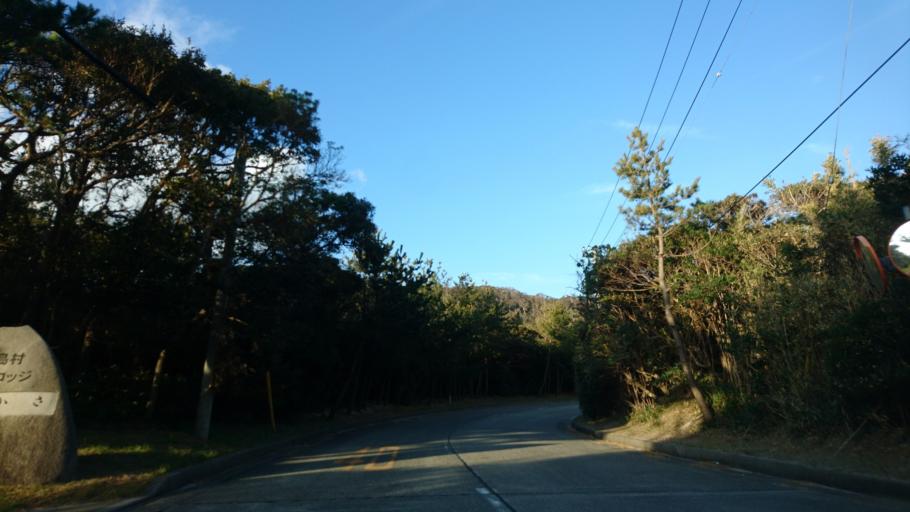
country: JP
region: Shizuoka
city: Shimoda
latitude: 34.3608
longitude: 139.2479
